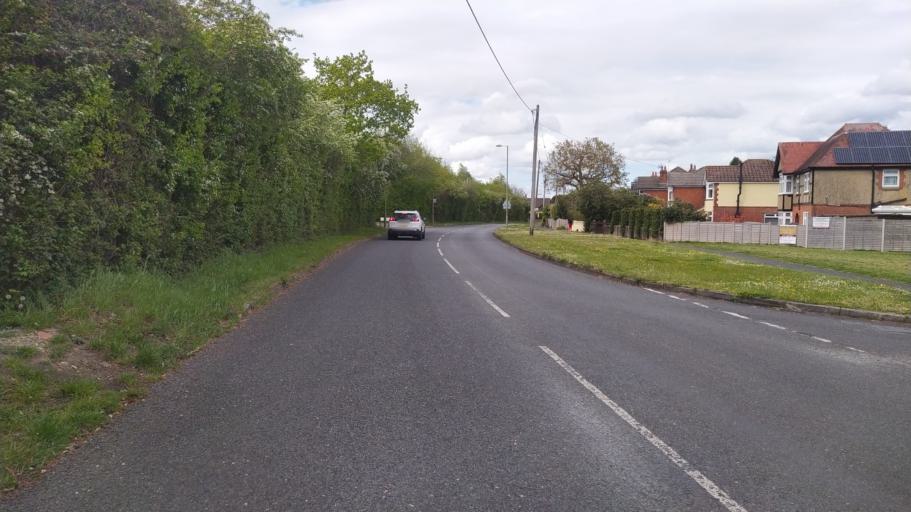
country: GB
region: England
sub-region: Hampshire
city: Totton
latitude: 50.9261
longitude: -1.5209
